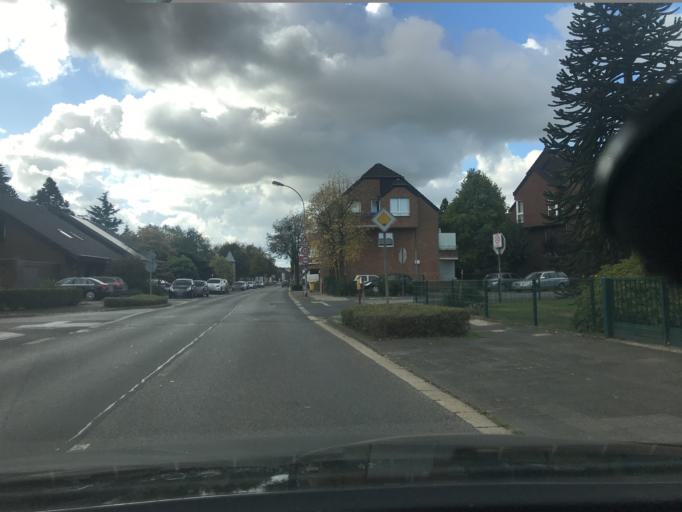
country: DE
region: North Rhine-Westphalia
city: Tonisvorst
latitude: 51.3271
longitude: 6.4938
